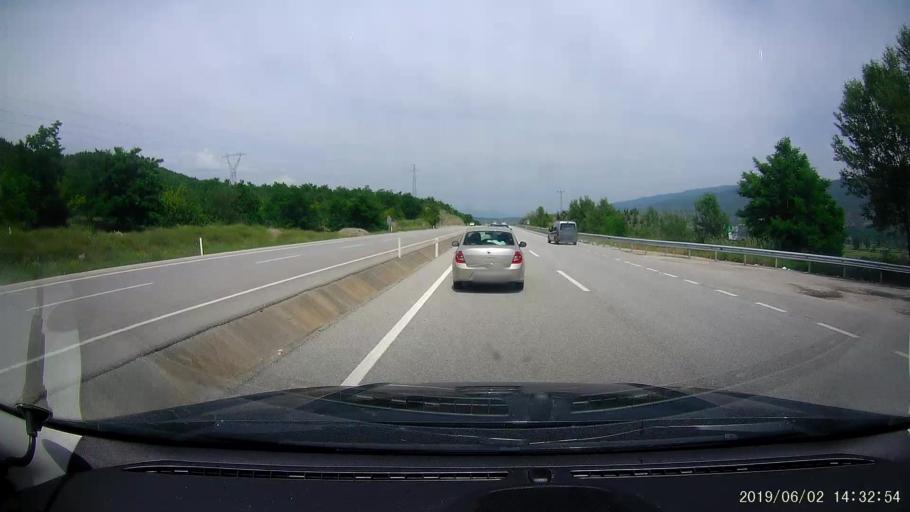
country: TR
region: Kastamonu
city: Tosya
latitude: 41.0277
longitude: 34.1579
